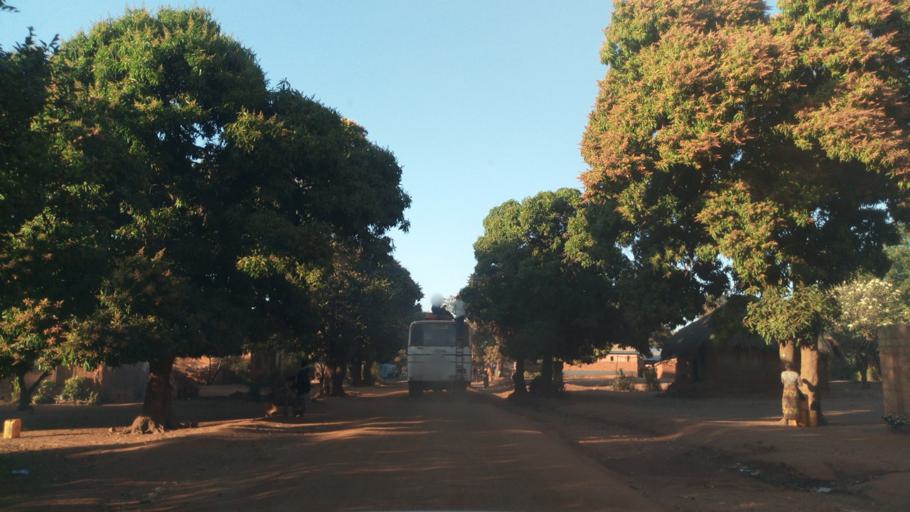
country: ZM
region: Luapula
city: Mwense
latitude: -10.3776
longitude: 28.6141
